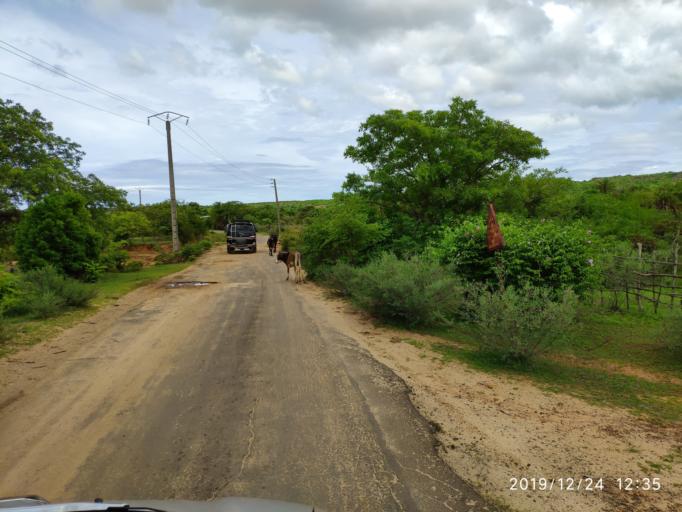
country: MG
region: Diana
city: Antsiranana
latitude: -12.3119
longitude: 49.3446
